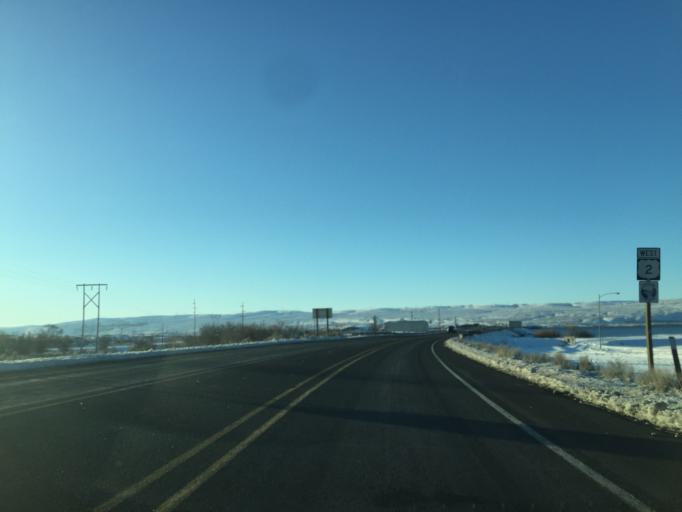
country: US
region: Washington
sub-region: Grant County
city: Soap Lake
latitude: 47.6158
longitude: -119.2945
